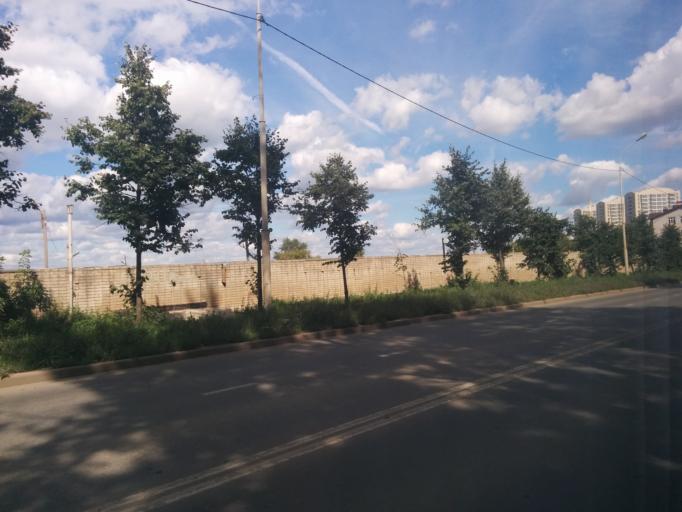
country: RU
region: Tatarstan
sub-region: Gorod Kazan'
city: Kazan
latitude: 55.7955
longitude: 49.1981
